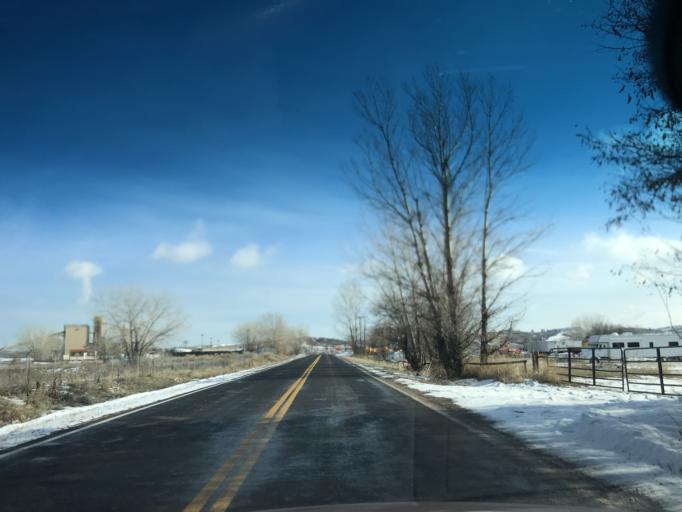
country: US
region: Colorado
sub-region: Douglas County
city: Highlands Ranch
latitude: 39.4710
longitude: -104.9963
